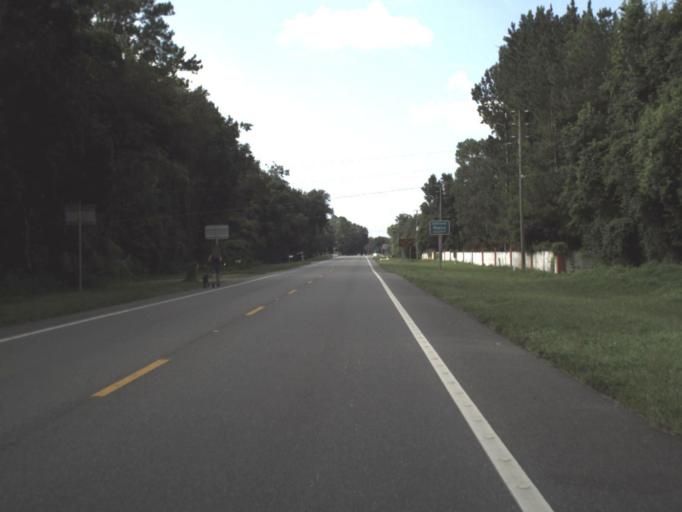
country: US
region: Florida
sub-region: Pasco County
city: Lacoochee
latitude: 28.4791
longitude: -82.1961
